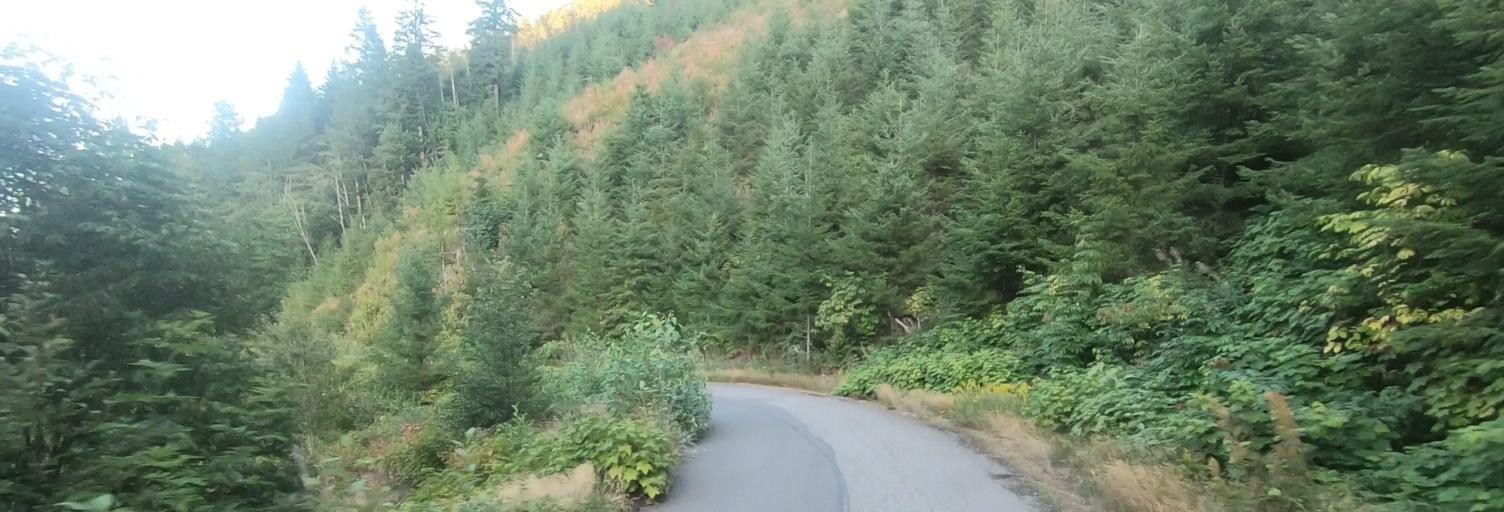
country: US
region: Washington
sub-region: Whatcom County
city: Peaceful Valley
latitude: 48.9246
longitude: -121.9576
